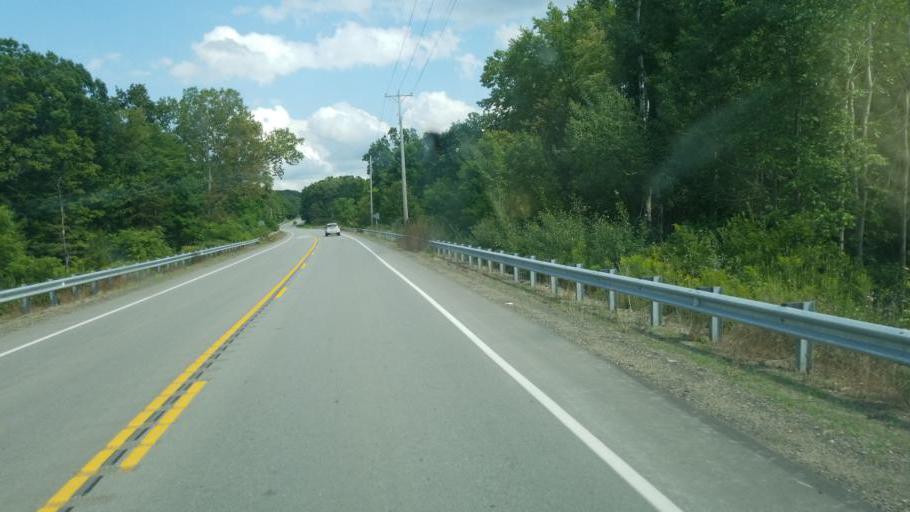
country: US
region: Pennsylvania
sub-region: Crawford County
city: Linesville
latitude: 41.6054
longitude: -80.3806
